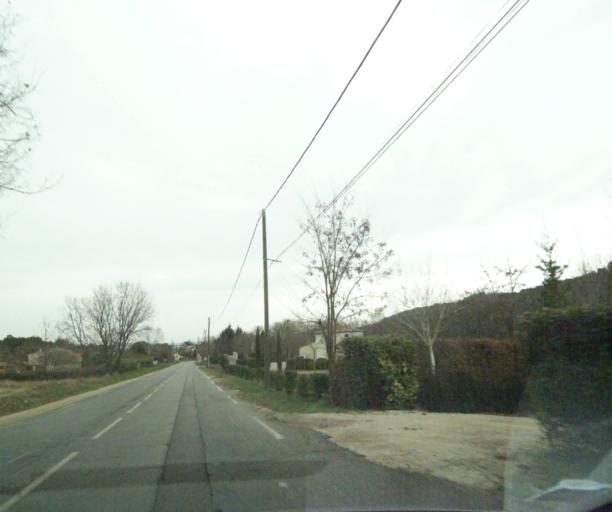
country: FR
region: Provence-Alpes-Cote d'Azur
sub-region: Departement des Bouches-du-Rhone
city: Le Puy-Sainte-Reparade
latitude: 43.6585
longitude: 5.4091
